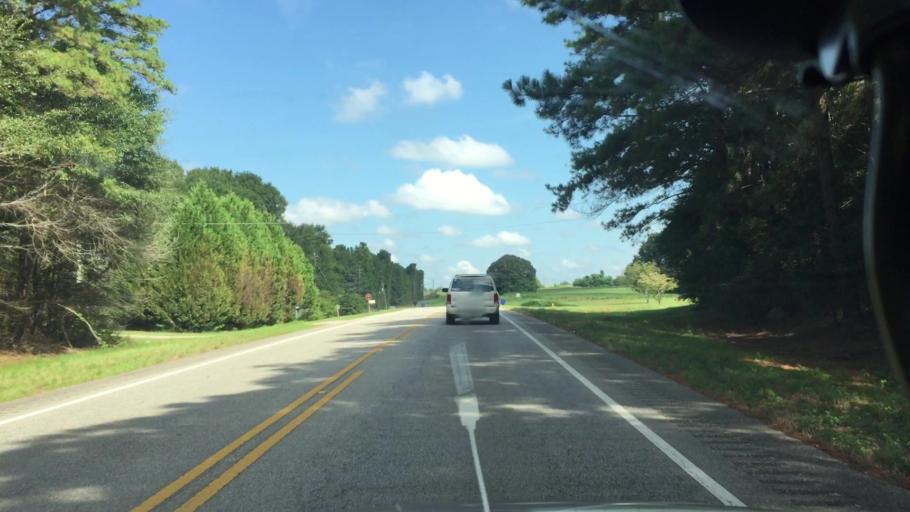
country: US
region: Alabama
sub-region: Coffee County
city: New Brockton
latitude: 31.4100
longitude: -85.8833
